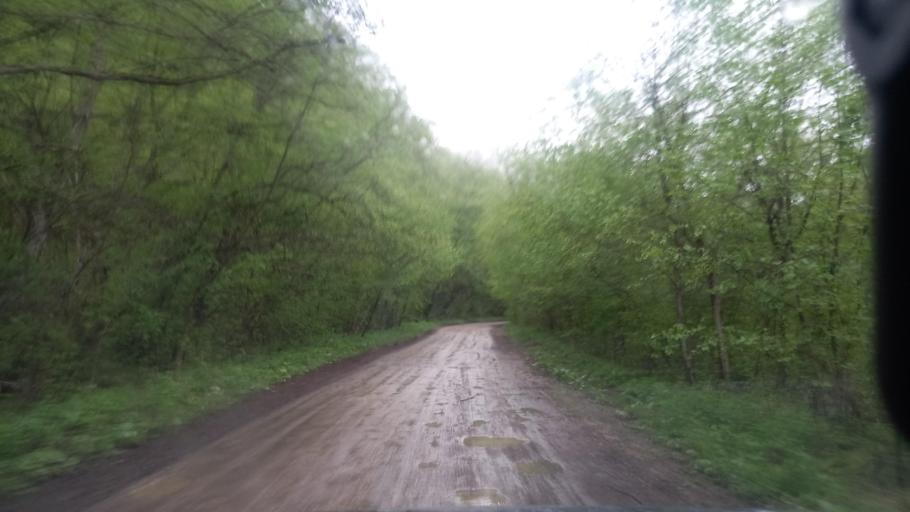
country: RU
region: Kabardino-Balkariya
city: Gundelen
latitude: 43.5782
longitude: 43.0986
